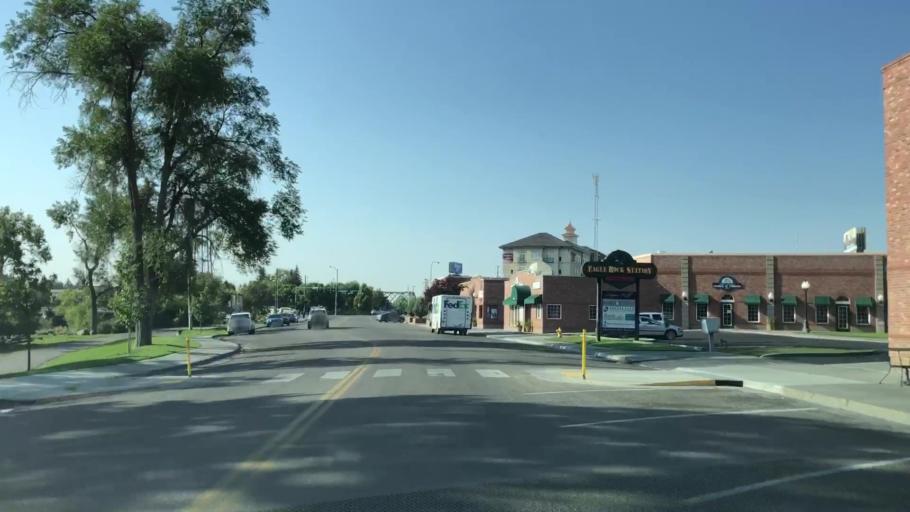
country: US
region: Idaho
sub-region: Bonneville County
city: Idaho Falls
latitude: 43.4951
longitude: -112.0450
